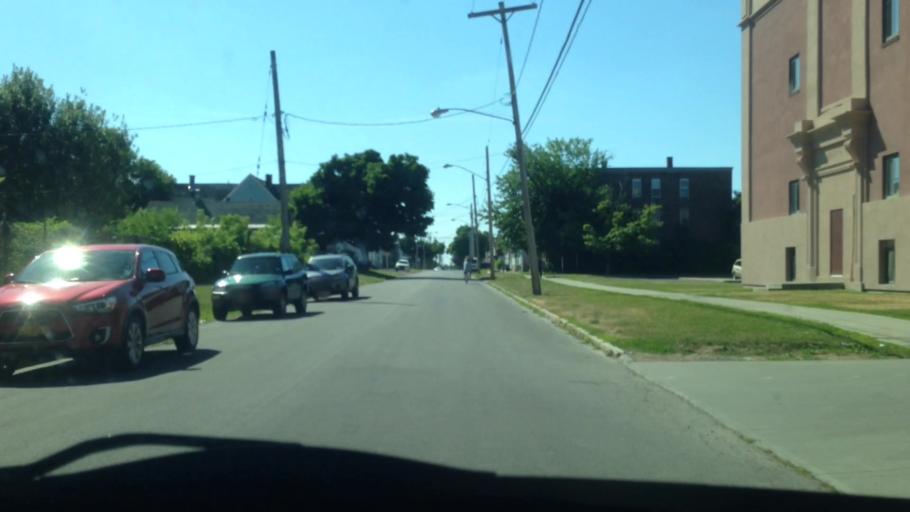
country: US
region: New York
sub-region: Oneida County
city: Utica
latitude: 43.0975
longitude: -75.2123
